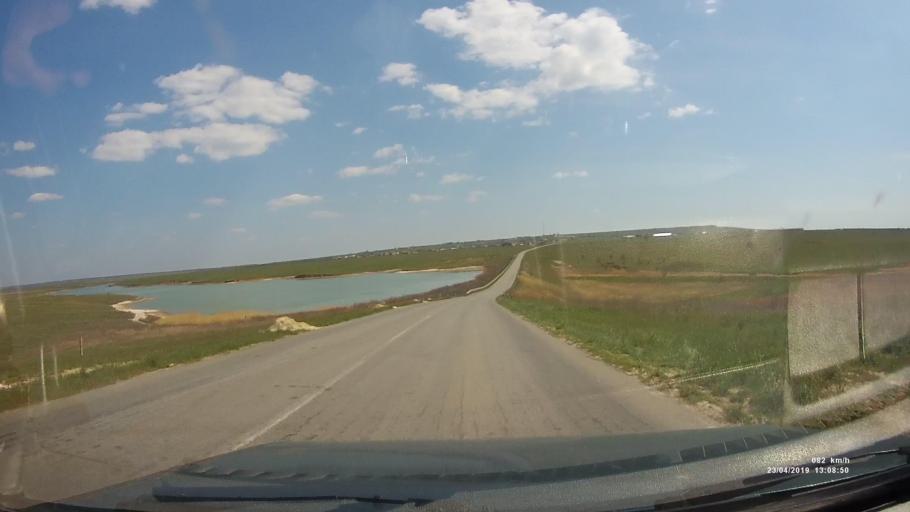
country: RU
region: Kalmykiya
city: Yashalta
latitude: 46.5795
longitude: 42.7821
